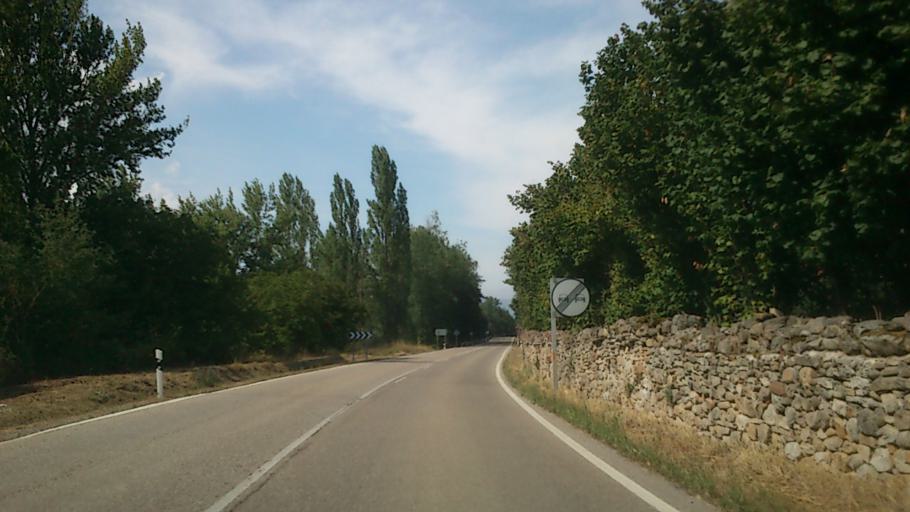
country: ES
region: Castille and Leon
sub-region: Provincia de Burgos
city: Medina de Pomar
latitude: 43.0151
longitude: -3.4833
